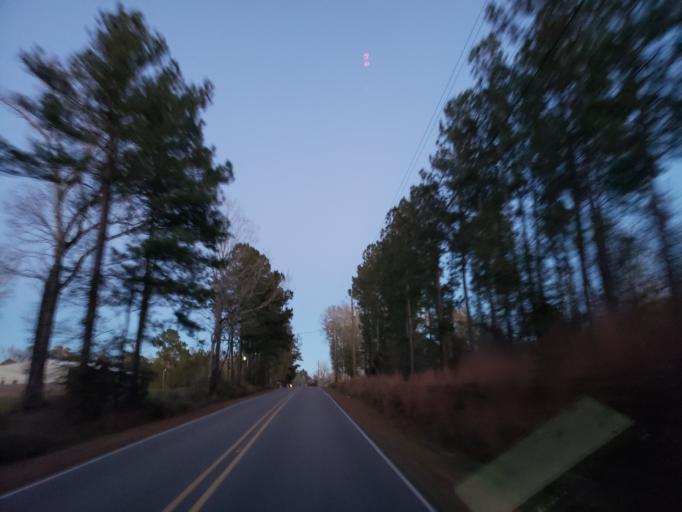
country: US
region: Mississippi
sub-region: Forrest County
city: Rawls Springs
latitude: 31.4233
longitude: -89.3457
